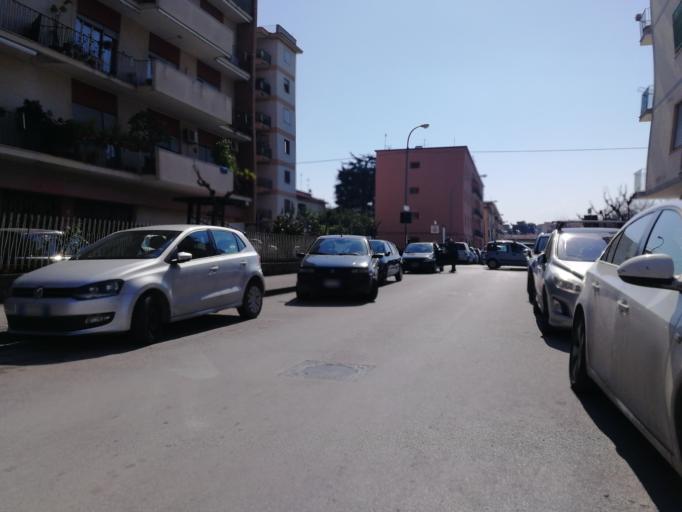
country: IT
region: Campania
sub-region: Provincia di Caserta
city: Santa Maria Capua Vetere
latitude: 41.0864
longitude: 14.2574
